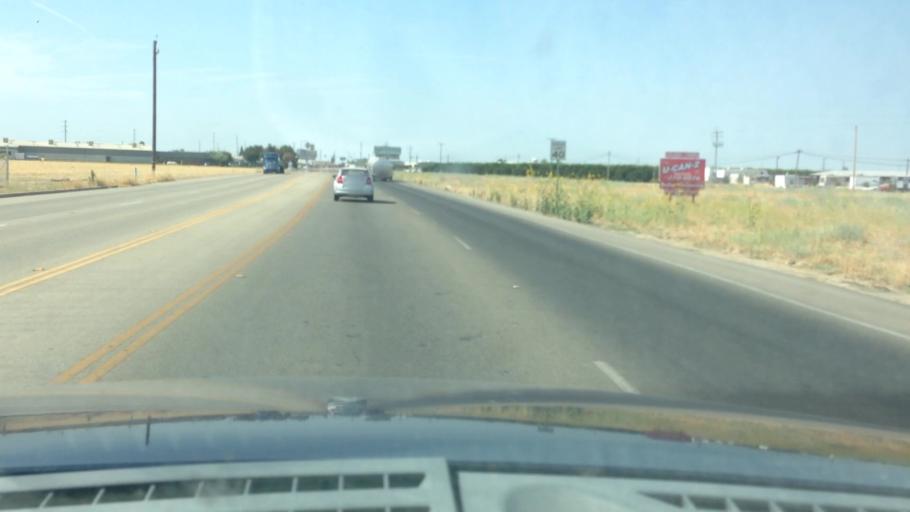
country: US
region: California
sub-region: Fresno County
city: Sanger
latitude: 36.6894
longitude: -119.5550
